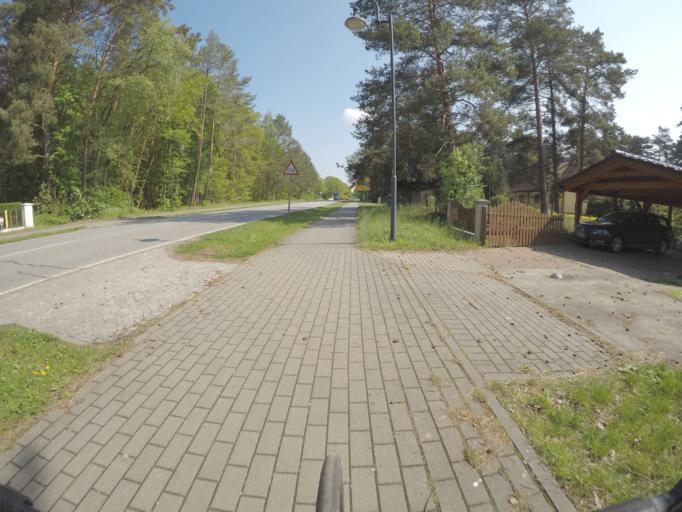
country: DE
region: Brandenburg
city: Wandlitz
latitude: 52.7407
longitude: 13.4564
